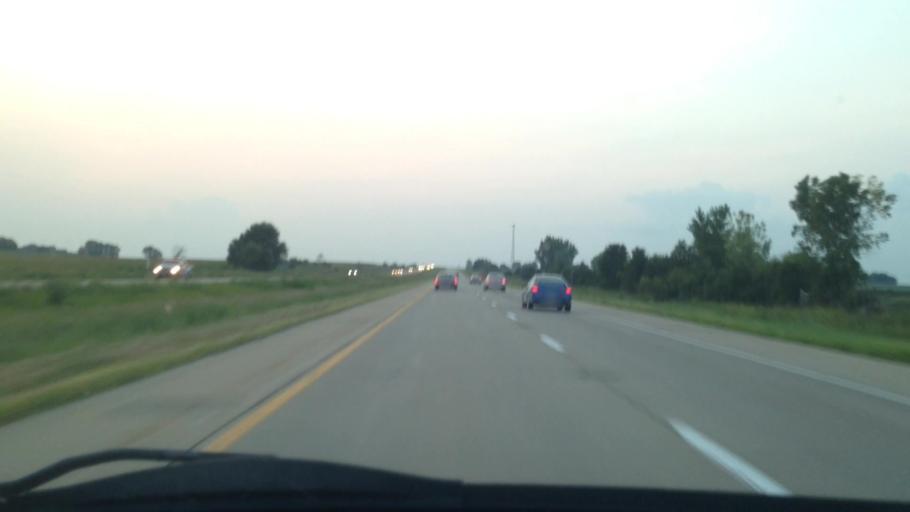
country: US
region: Iowa
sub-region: Benton County
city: Urbana
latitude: 42.3009
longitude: -91.9639
